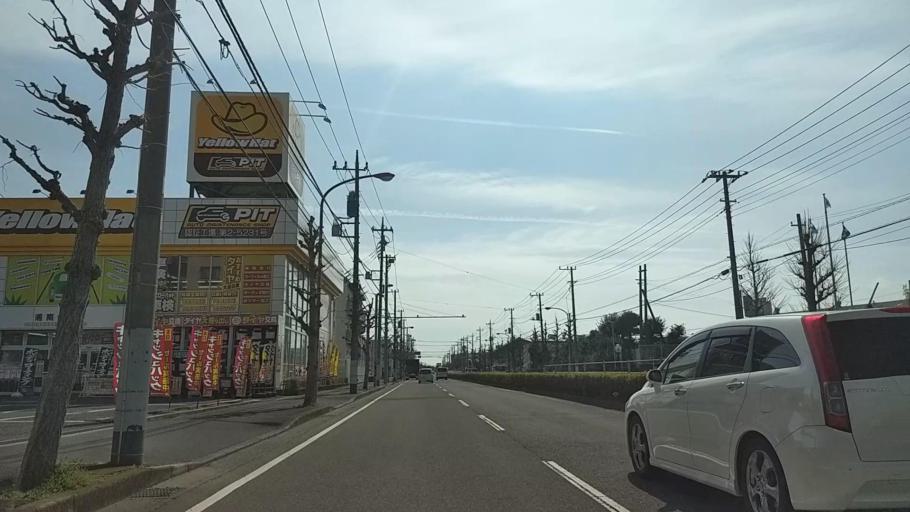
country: JP
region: Kanagawa
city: Fujisawa
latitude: 35.3916
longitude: 139.4577
